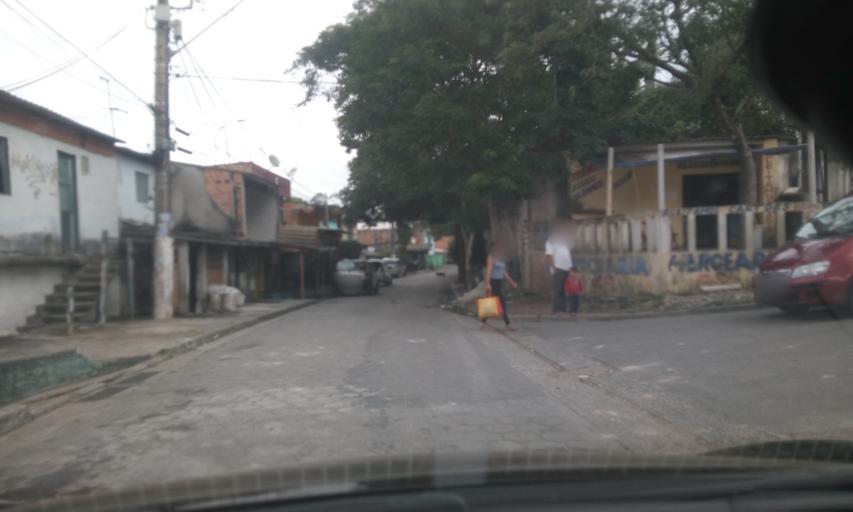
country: BR
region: Sao Paulo
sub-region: Diadema
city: Diadema
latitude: -23.7685
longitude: -46.6096
